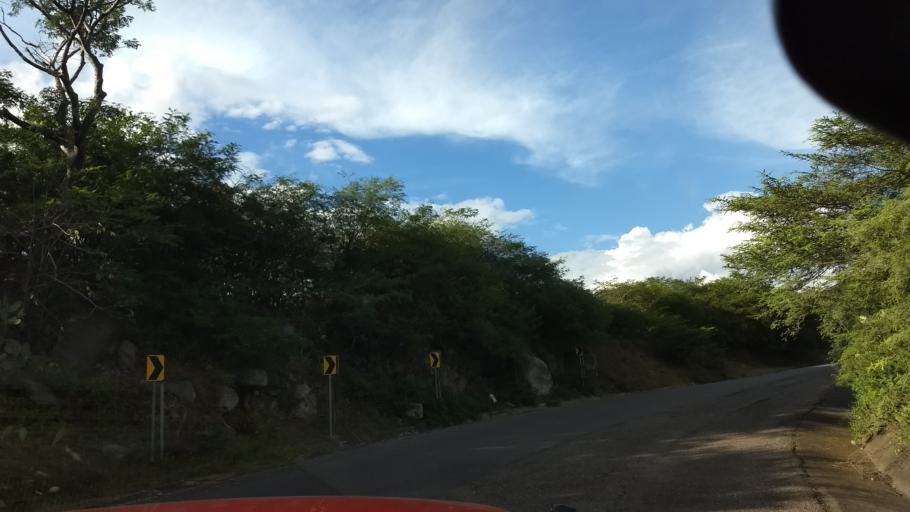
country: MX
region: Colima
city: Suchitlan
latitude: 19.4644
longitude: -103.8263
